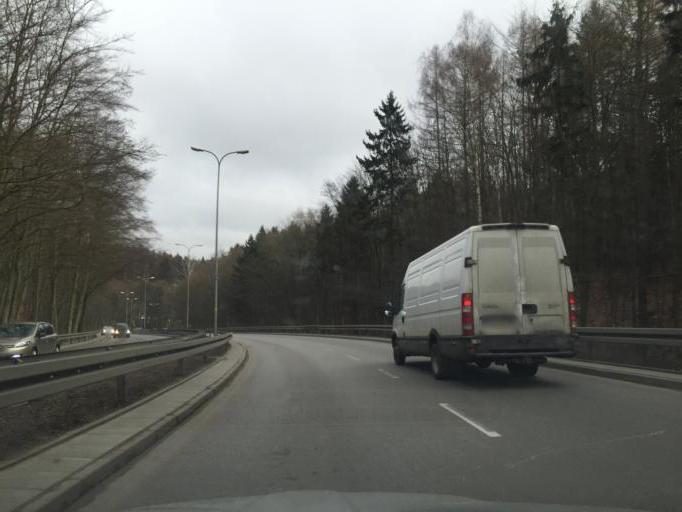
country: PL
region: Pomeranian Voivodeship
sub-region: Powiat gdanski
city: Kowale
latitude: 54.3721
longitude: 18.5484
